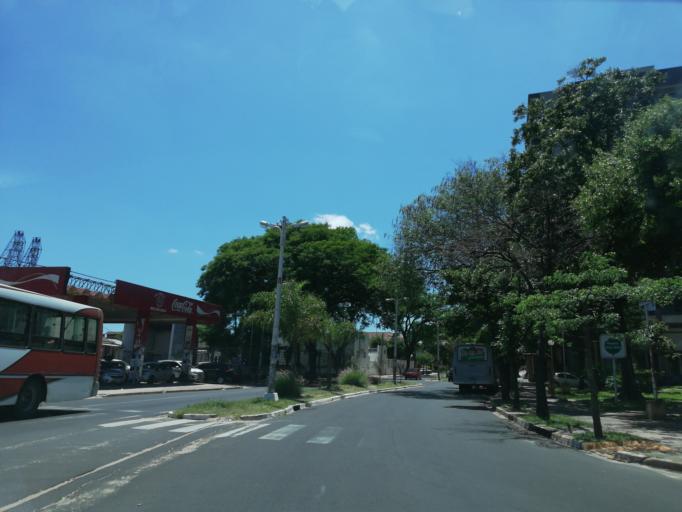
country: AR
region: Corrientes
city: Corrientes
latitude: -27.4613
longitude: -58.8351
